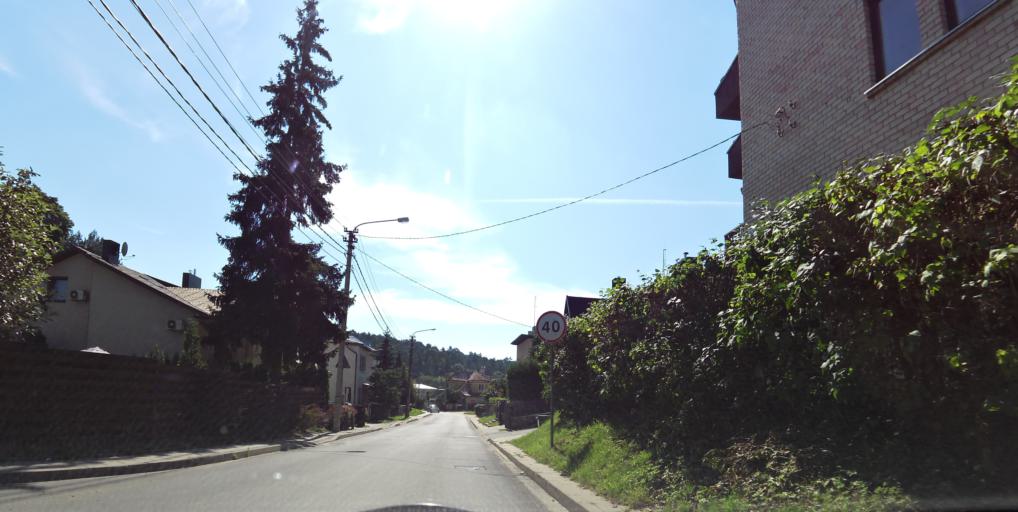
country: LT
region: Vilnius County
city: Rasos
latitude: 54.6880
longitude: 25.3222
